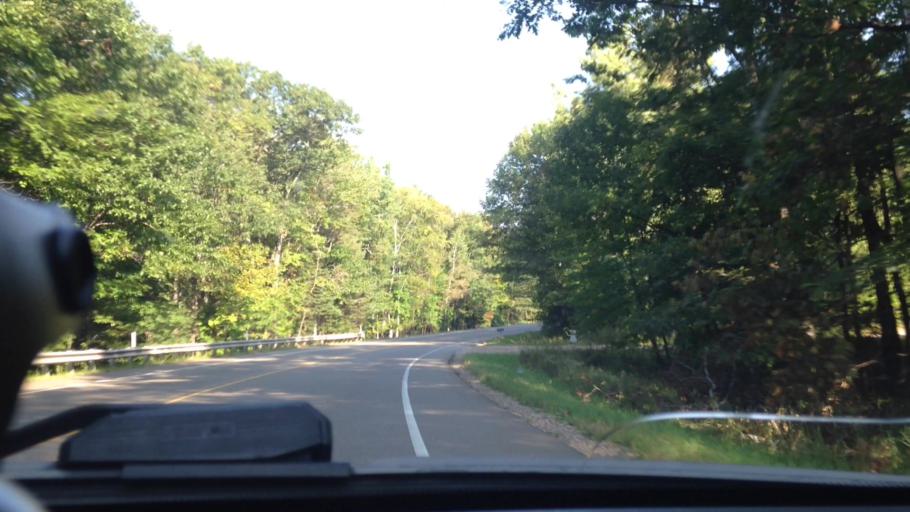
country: US
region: Michigan
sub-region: Dickinson County
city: Quinnesec
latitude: 45.8233
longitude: -87.9914
